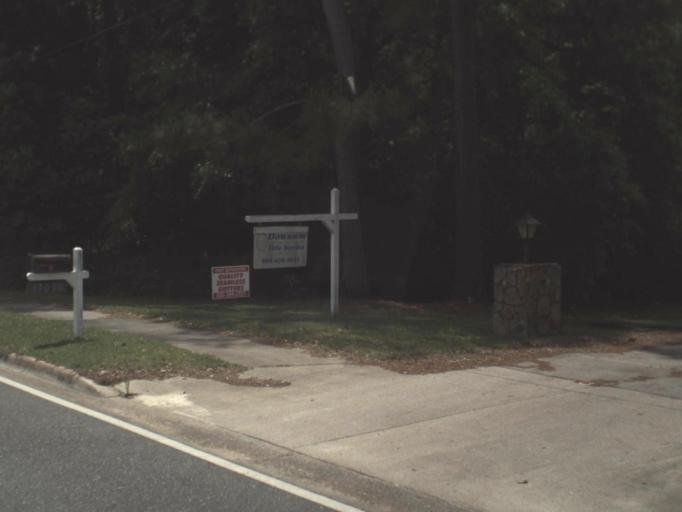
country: US
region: Florida
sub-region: Calhoun County
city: Blountstown
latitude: 30.4408
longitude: -85.0459
